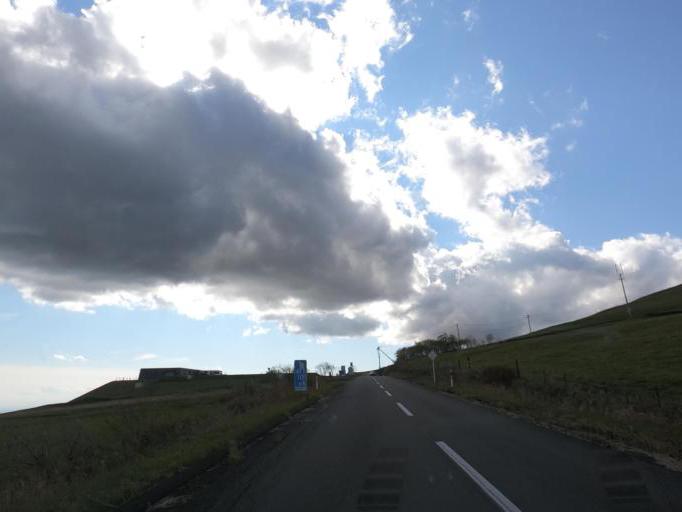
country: JP
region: Hokkaido
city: Otofuke
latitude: 43.2880
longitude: 143.1863
